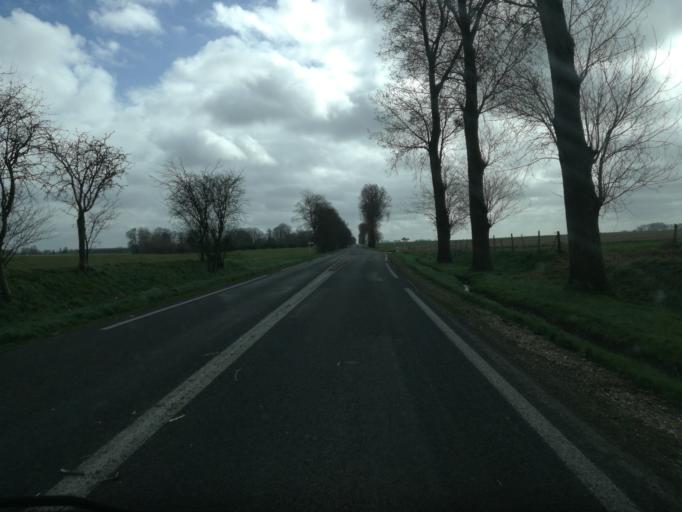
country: FR
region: Haute-Normandie
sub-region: Departement de la Seine-Maritime
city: Fauville-en-Caux
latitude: 49.6459
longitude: 0.6135
